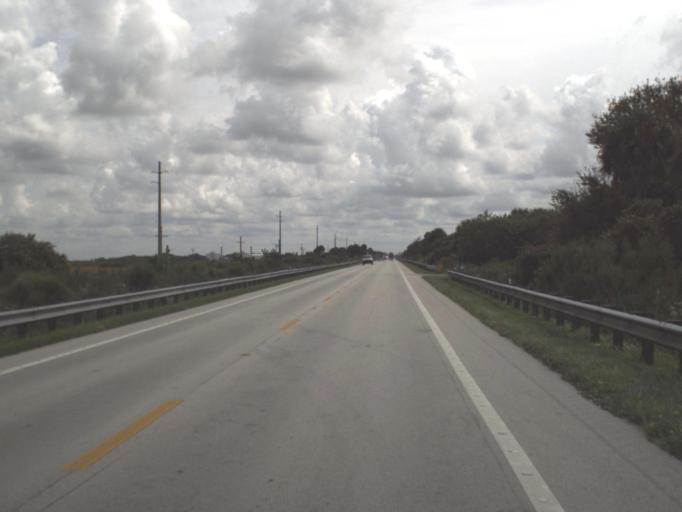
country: US
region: Florida
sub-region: Glades County
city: Buckhead Ridge
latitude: 27.2361
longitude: -81.0593
